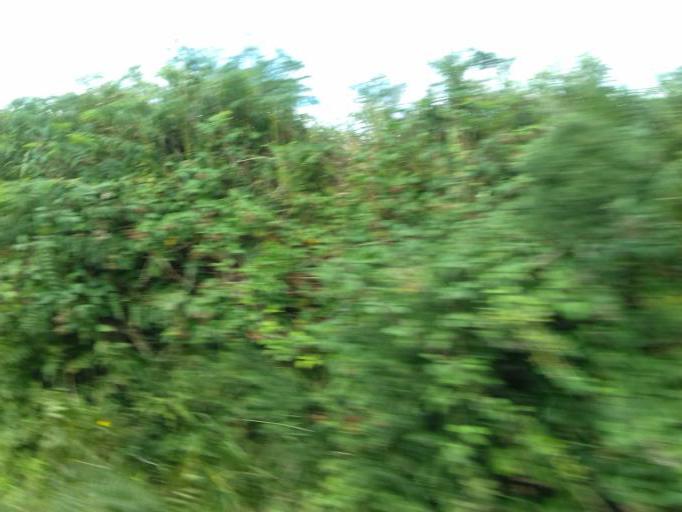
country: IE
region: Leinster
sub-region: Loch Garman
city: Ballinroad
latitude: 52.4866
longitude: -6.4447
